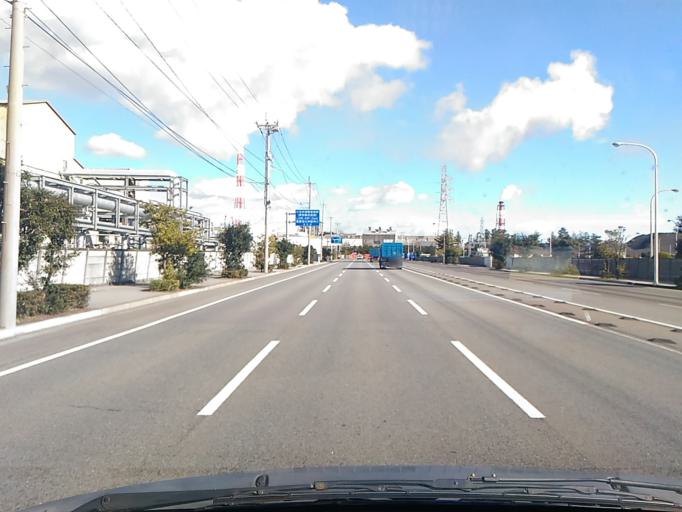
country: JP
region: Fukushima
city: Iwaki
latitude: 36.9380
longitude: 140.8755
